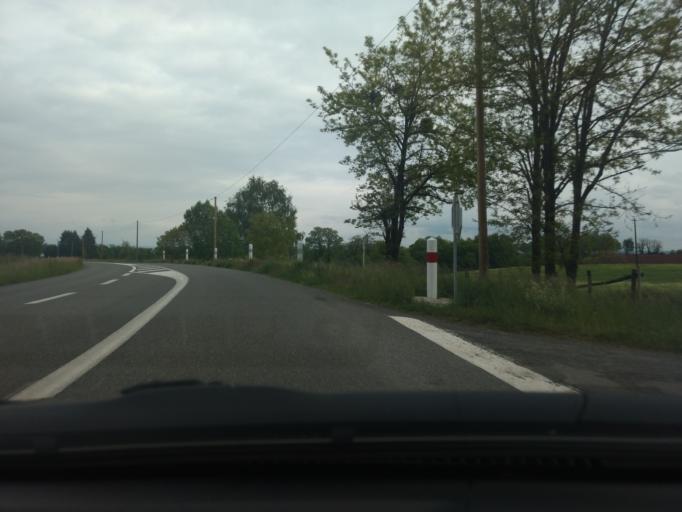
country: FR
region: Midi-Pyrenees
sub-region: Departement de l'Aveyron
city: Viviez
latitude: 44.5436
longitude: 2.1664
